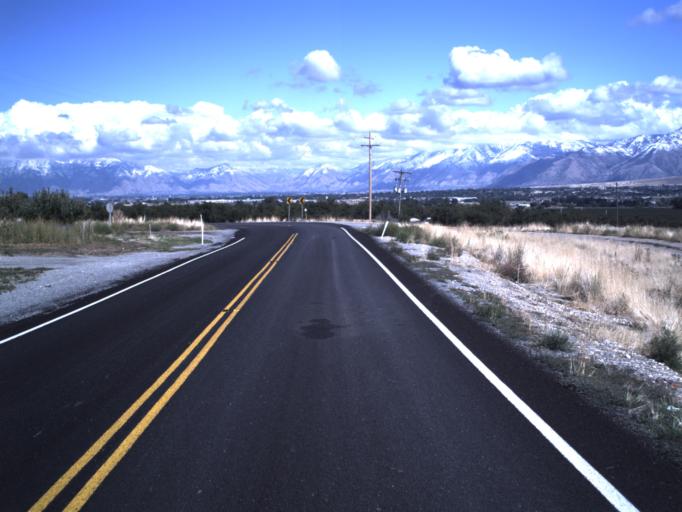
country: US
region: Utah
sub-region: Utah County
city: Santaquin
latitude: 40.0155
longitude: -111.7950
